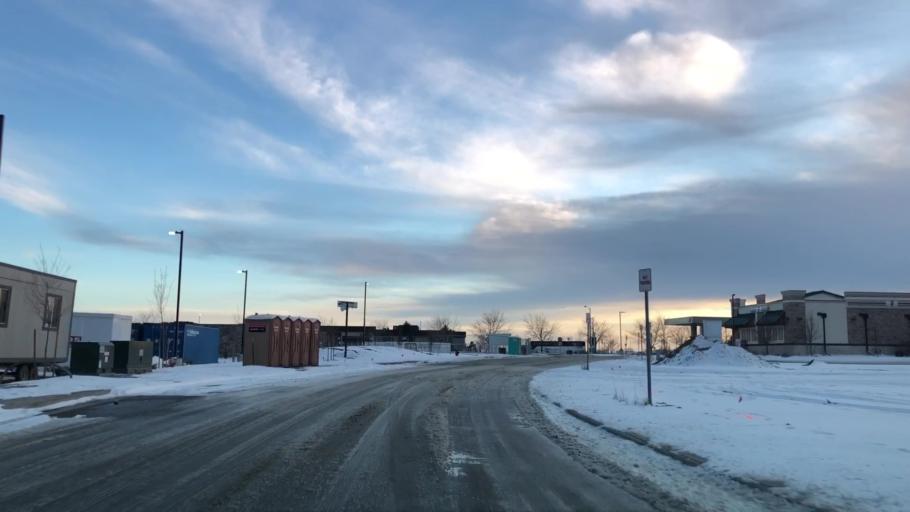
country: US
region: Colorado
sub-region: Weld County
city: Windsor
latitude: 40.4374
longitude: -104.9804
